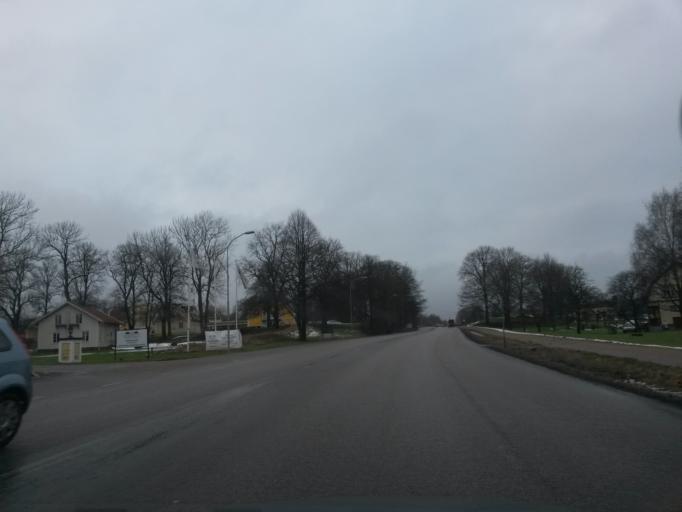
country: SE
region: Vaestra Goetaland
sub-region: Vanersborgs Kommun
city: Vargon
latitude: 58.3539
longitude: 12.3894
